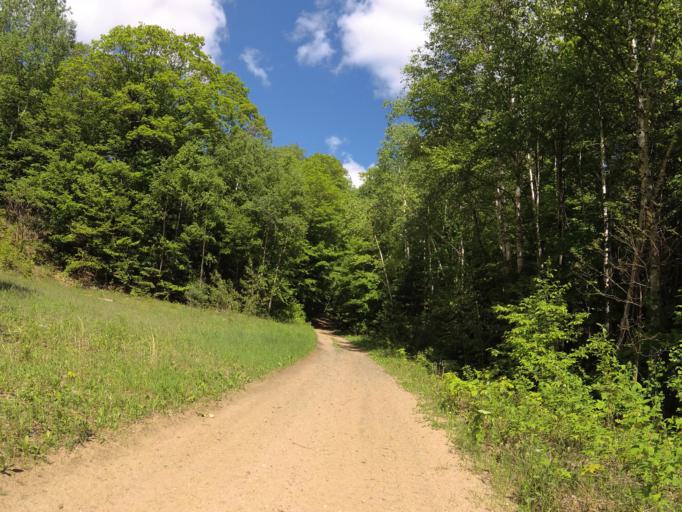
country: CA
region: Ontario
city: Renfrew
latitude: 45.0461
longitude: -76.8264
